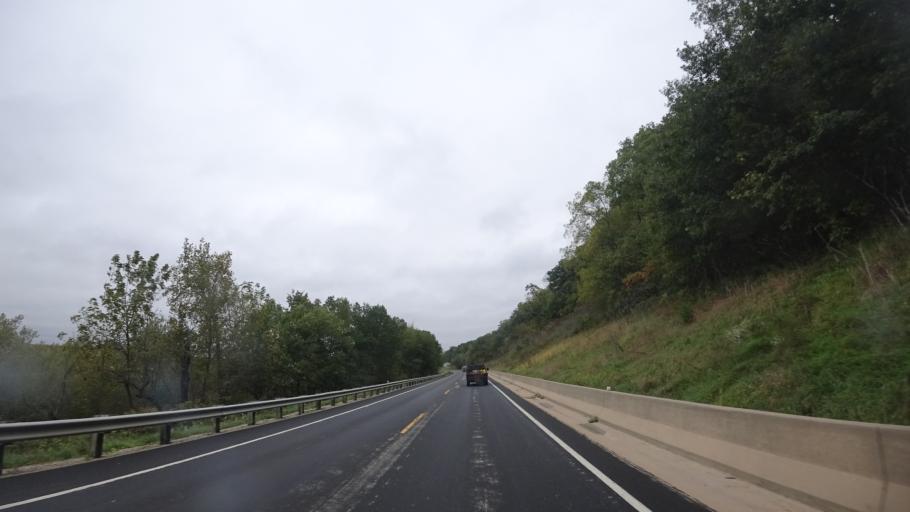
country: US
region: Wisconsin
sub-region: Grant County
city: Boscobel
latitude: 43.1218
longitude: -90.7785
